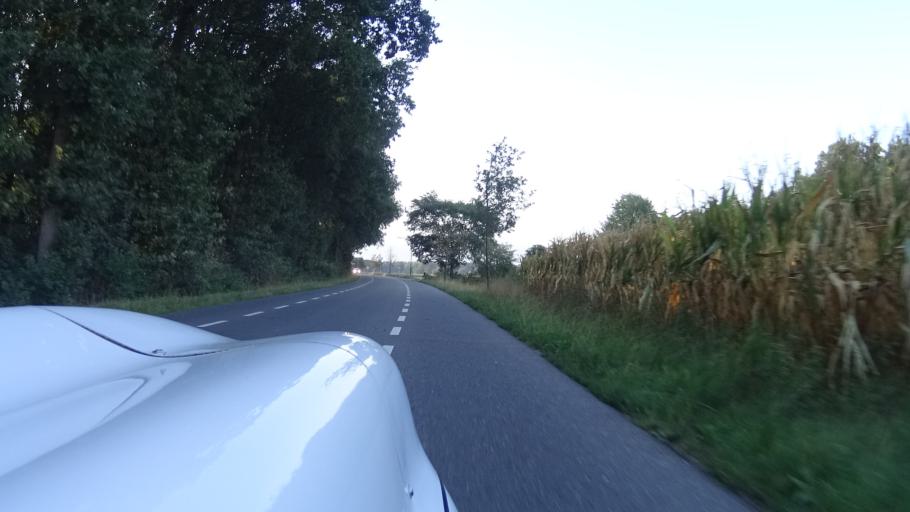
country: NL
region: Limburg
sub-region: Gemeente Venray
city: Venray
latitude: 51.5630
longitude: 6.0395
